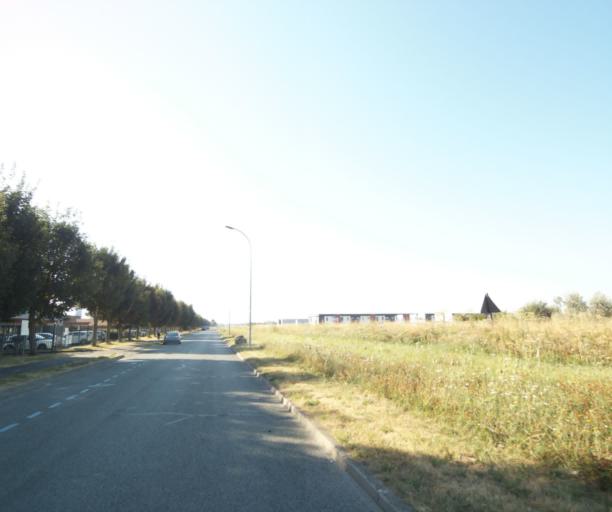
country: FR
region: Ile-de-France
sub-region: Departement de Seine-et-Marne
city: Lieusaint
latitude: 48.6222
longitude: 2.5637
